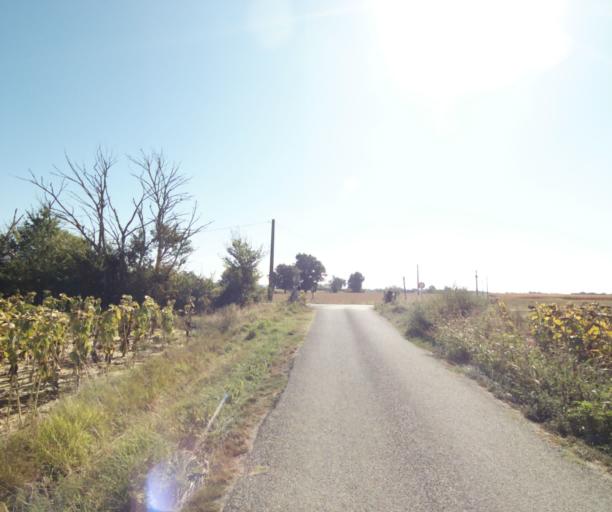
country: FR
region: Midi-Pyrenees
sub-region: Departement du Tarn-et-Garonne
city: Verdun-sur-Garonne
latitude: 43.8174
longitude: 1.2234
